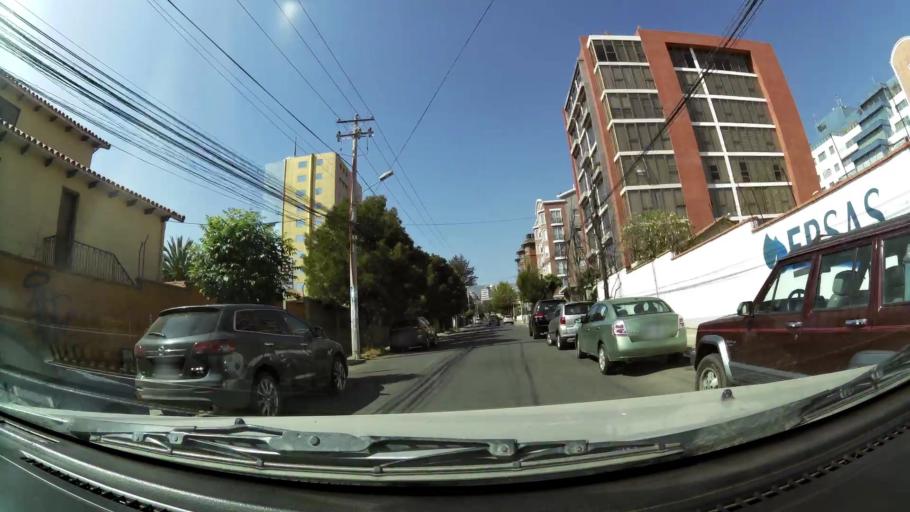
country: BO
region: La Paz
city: La Paz
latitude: -16.5395
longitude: -68.0818
